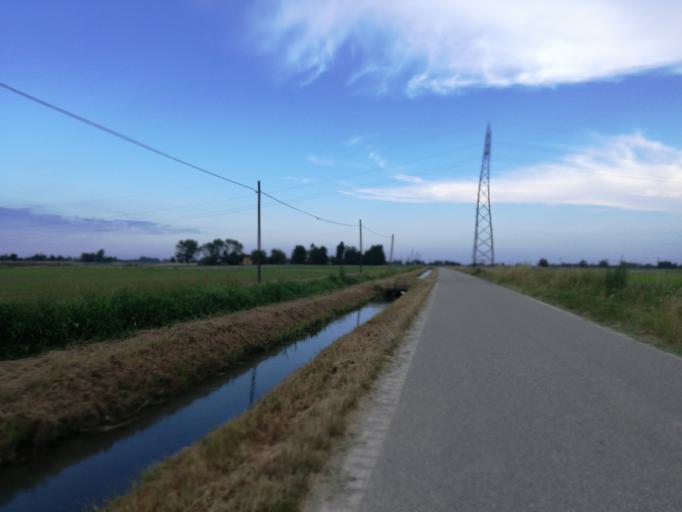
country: IT
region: Piedmont
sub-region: Provincia di Novara
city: Torrion Quartara
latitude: 45.4077
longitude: 8.6191
